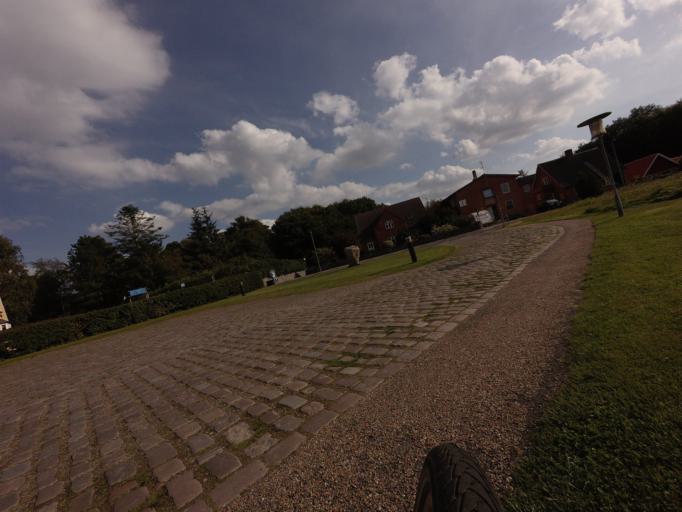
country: DK
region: Central Jutland
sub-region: Viborg Kommune
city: Karup
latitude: 56.3056
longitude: 9.1626
